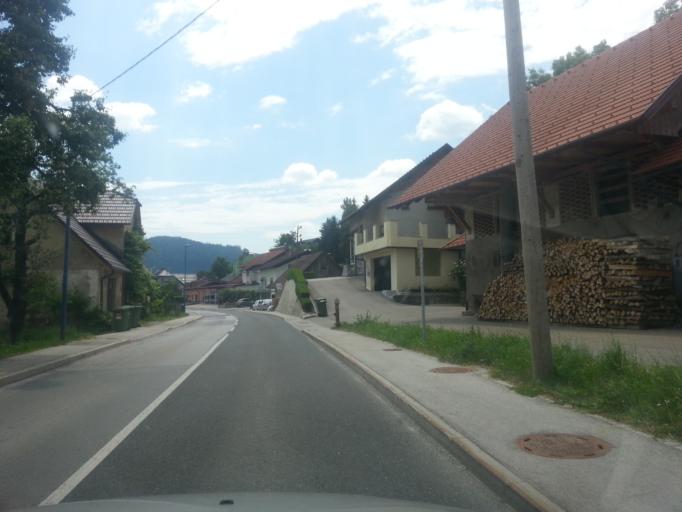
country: SI
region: Vrhnika
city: Vrhnika
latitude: 45.9717
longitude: 14.2934
